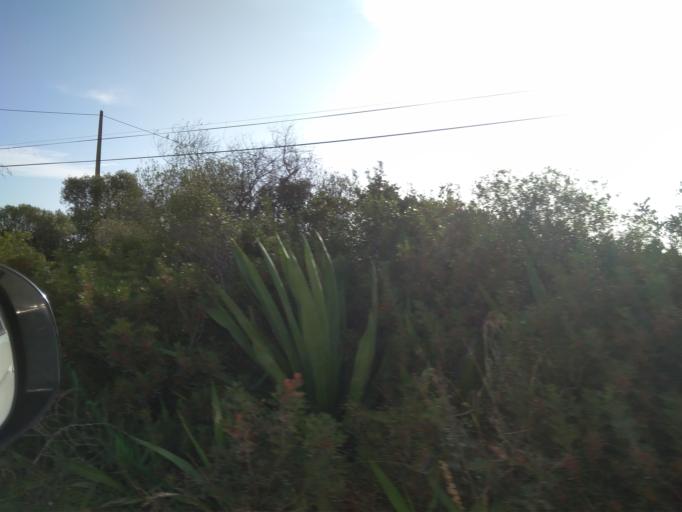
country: PT
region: Faro
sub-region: Faro
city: Santa Barbara de Nexe
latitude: 37.0941
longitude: -7.9463
